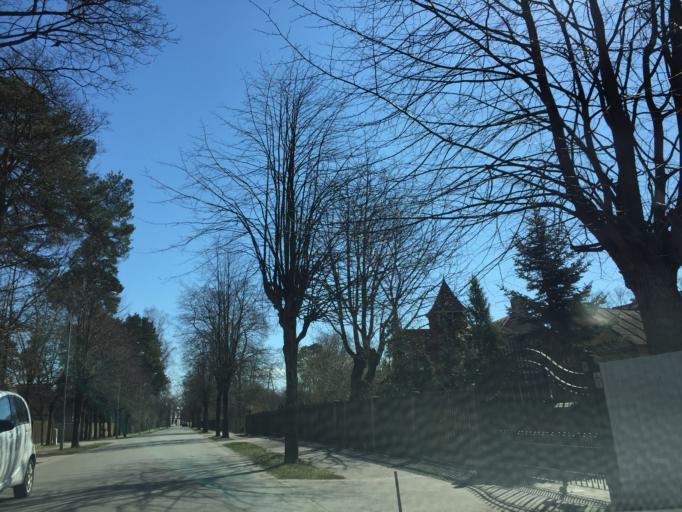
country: LV
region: Jurmala
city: Jurmala
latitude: 56.9686
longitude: 23.8159
